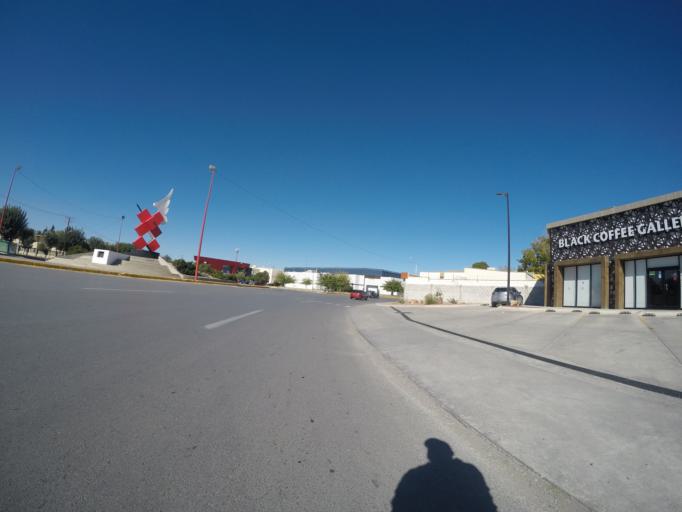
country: MX
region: Chihuahua
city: Ciudad Juarez
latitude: 31.7412
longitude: -106.4432
